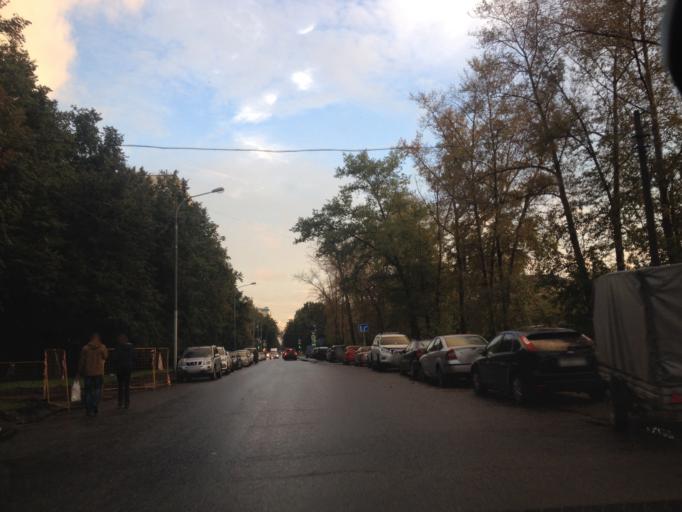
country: RU
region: Moscow
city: Metrogorodok
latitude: 55.8048
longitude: 37.8049
